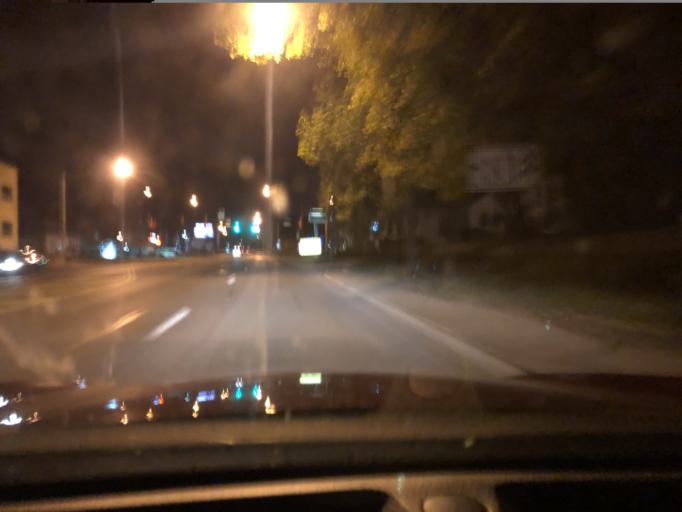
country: US
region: Ohio
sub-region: Logan County
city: Bellefontaine
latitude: 40.3480
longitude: -83.7612
